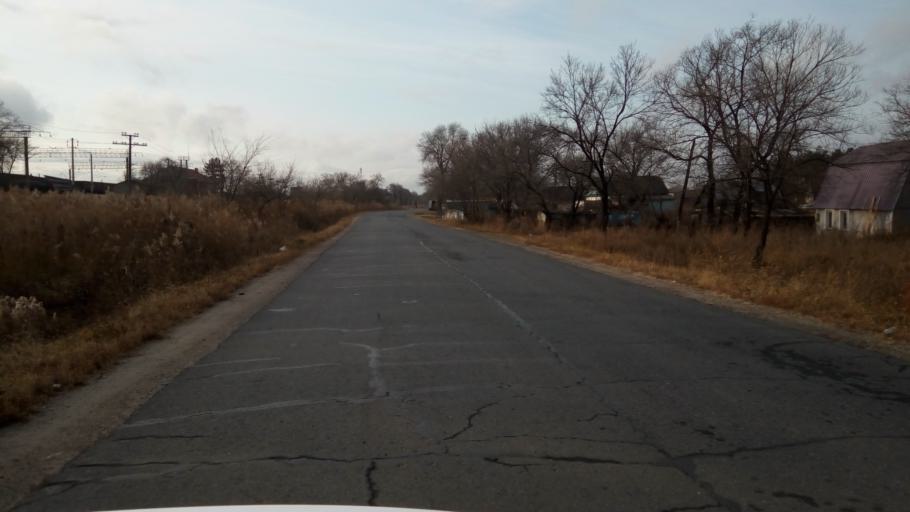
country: RU
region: Primorskiy
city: Ussuriysk
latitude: 43.7996
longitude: 131.9514
